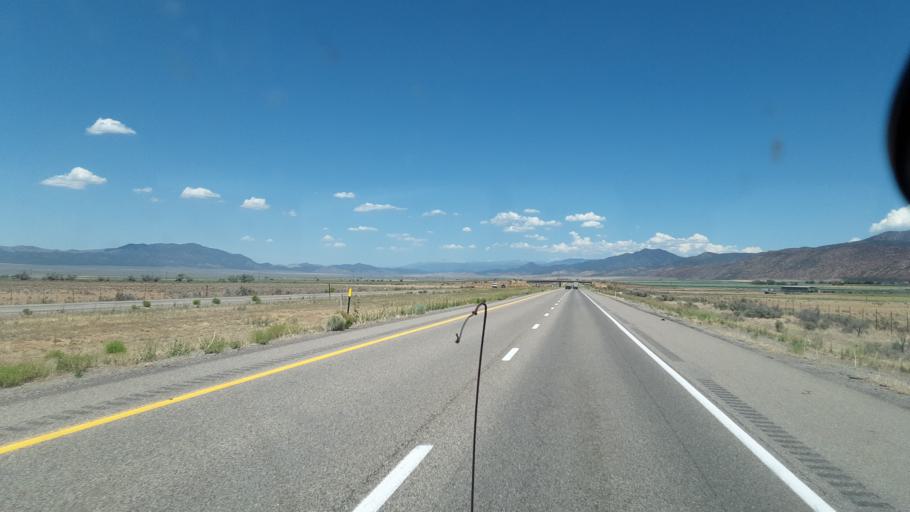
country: US
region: Utah
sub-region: Iron County
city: Parowan
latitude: 37.8759
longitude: -112.8097
